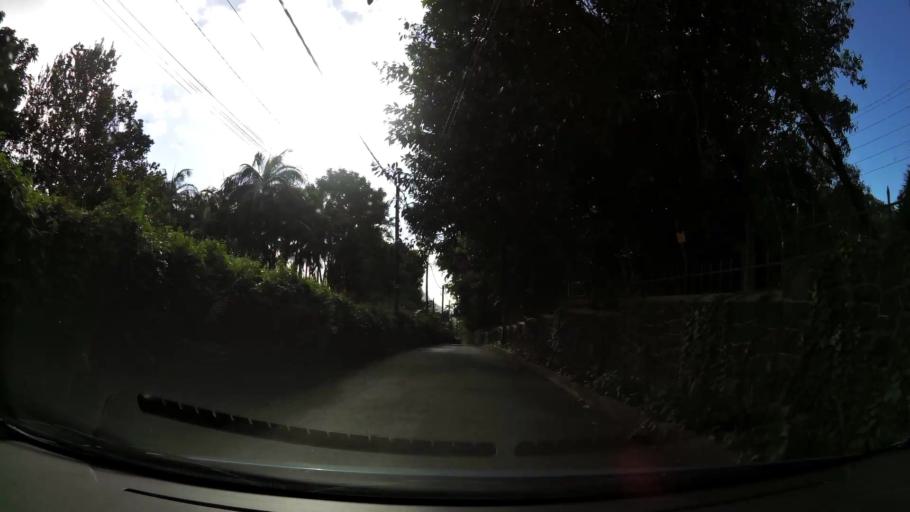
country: MU
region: Plaines Wilhems
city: Curepipe
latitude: -20.3170
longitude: 57.5001
